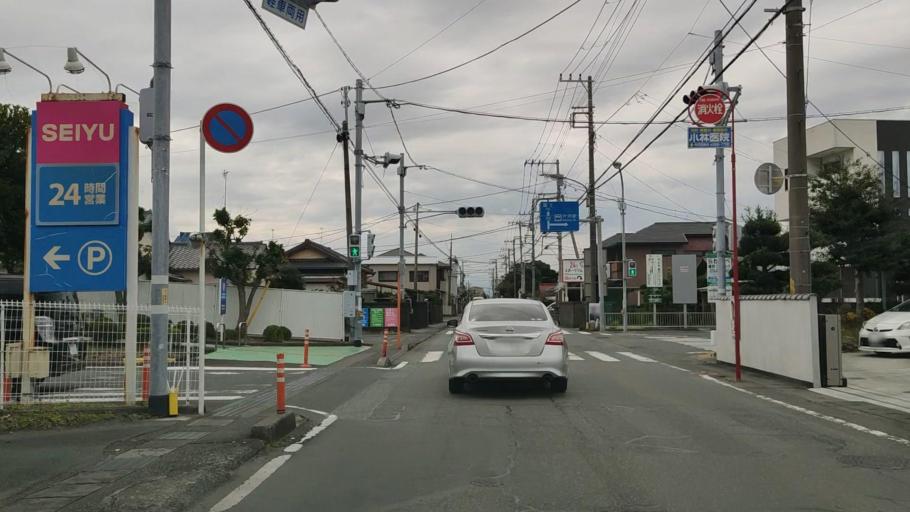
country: JP
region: Shizuoka
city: Numazu
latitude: 35.1163
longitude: 138.8191
